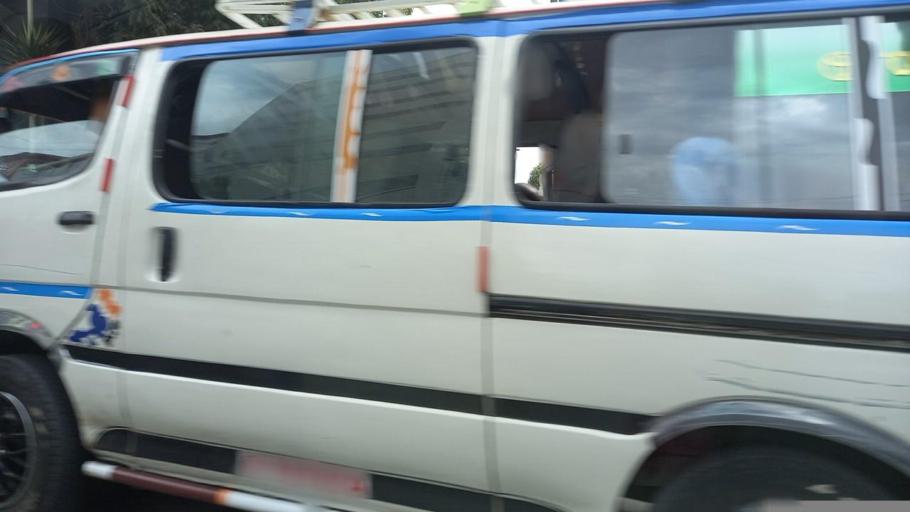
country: ET
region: Adis Abeba
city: Addis Ababa
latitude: 9.0204
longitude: 38.7993
